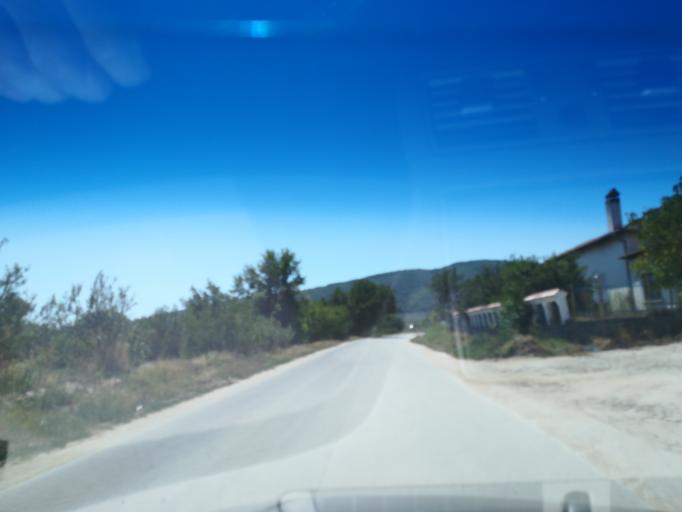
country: BG
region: Pazardzhik
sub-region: Obshtina Strelcha
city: Strelcha
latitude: 42.4980
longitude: 24.3190
